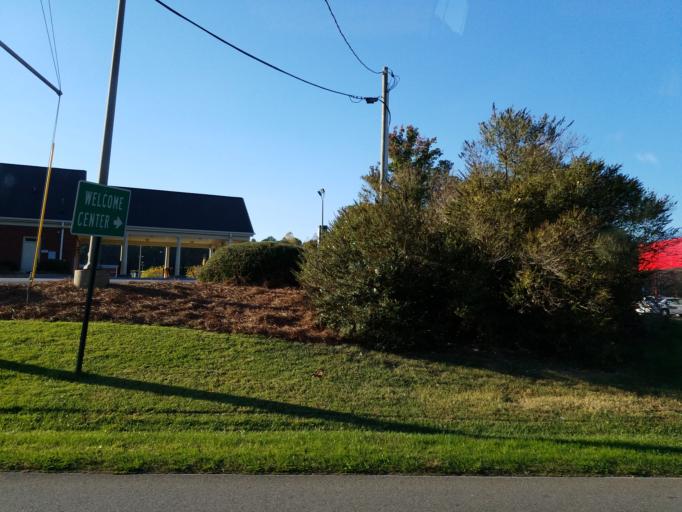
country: US
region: Georgia
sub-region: Gilmer County
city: Ellijay
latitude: 34.6776
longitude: -84.4767
